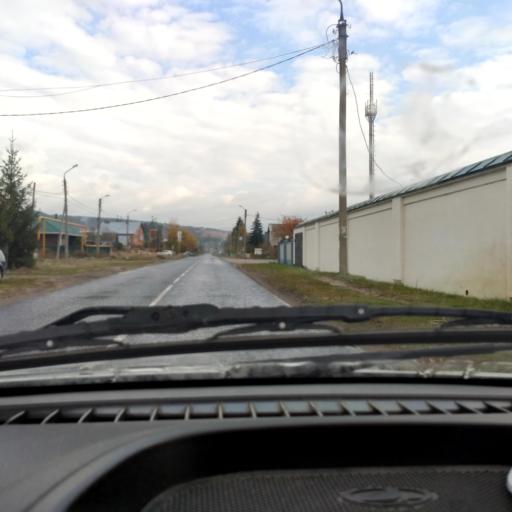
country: RU
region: Samara
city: Zhigulevsk
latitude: 53.4645
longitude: 49.6304
